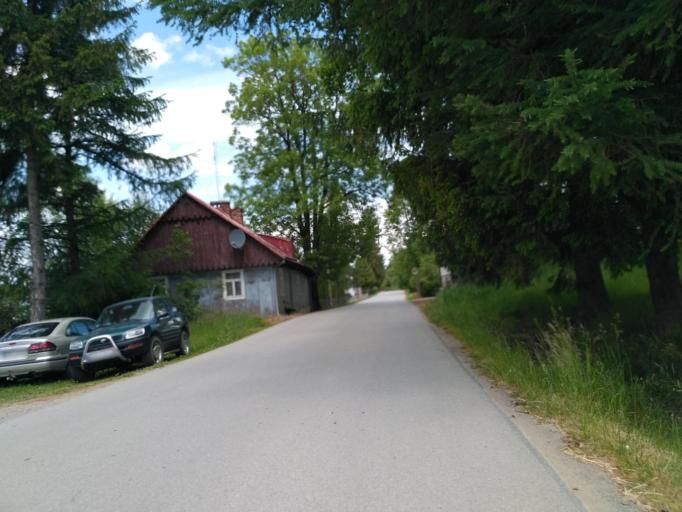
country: PL
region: Subcarpathian Voivodeship
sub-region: Powiat krosnienski
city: Dukla
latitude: 49.5887
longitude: 21.6216
